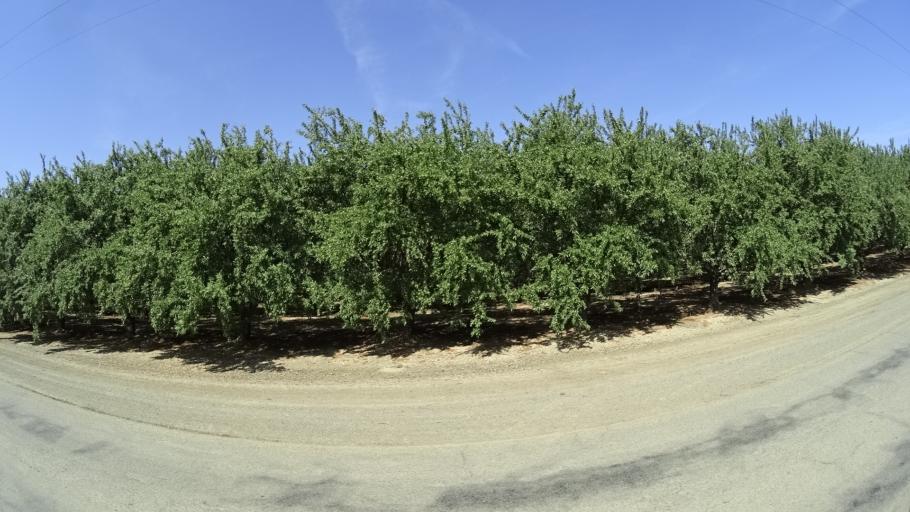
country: US
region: California
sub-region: Kings County
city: Kettleman City
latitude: 36.0875
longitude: -120.0037
